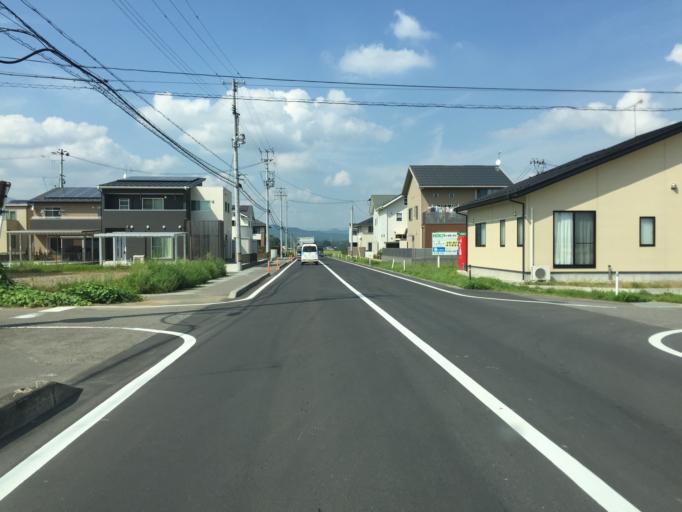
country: JP
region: Fukushima
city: Motomiya
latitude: 37.5471
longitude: 140.3842
